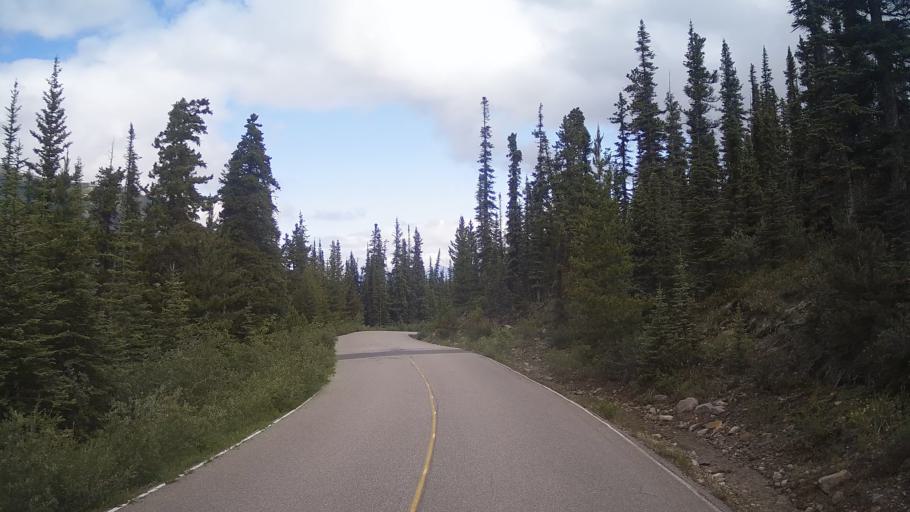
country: CA
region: Alberta
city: Jasper Park Lodge
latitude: 52.7102
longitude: -118.0562
